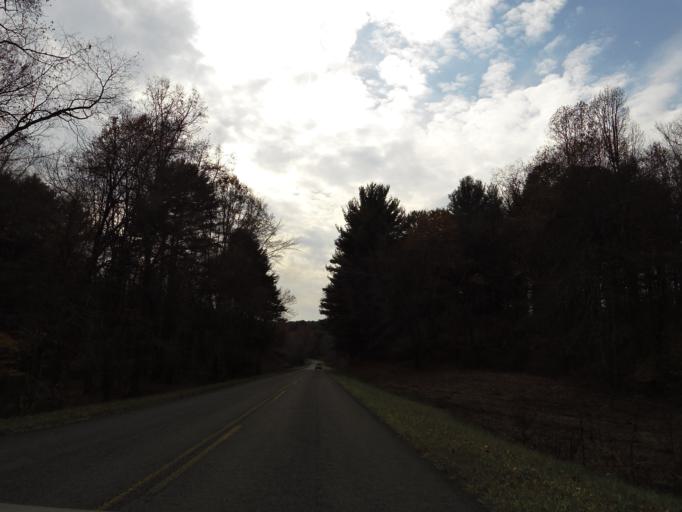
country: US
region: Virginia
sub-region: City of Galax
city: Galax
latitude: 36.6017
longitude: -80.8372
